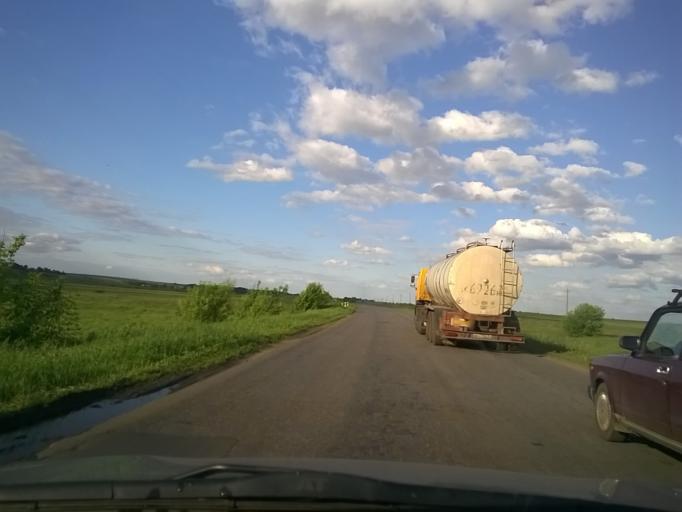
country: RU
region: Volgograd
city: Uryupinsk
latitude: 50.8245
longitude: 42.0598
